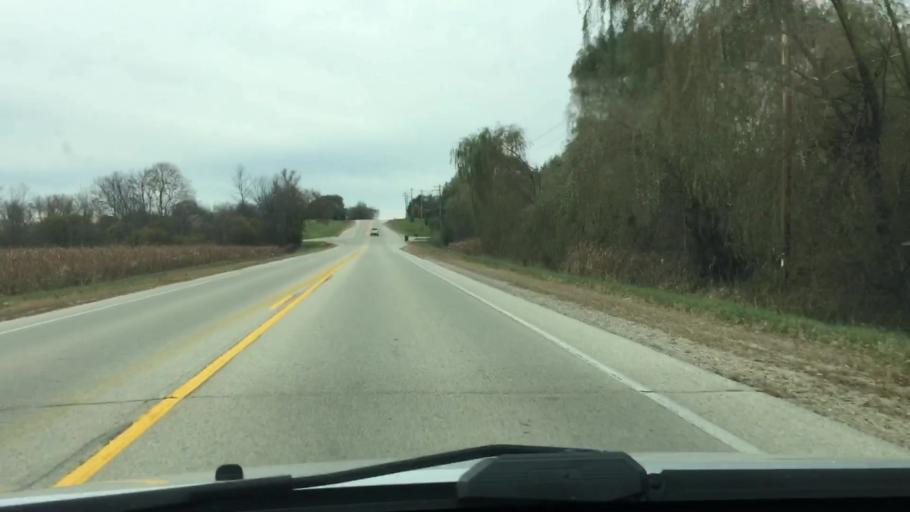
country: US
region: Wisconsin
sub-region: Waukesha County
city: Mukwonago
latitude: 42.8903
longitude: -88.2799
